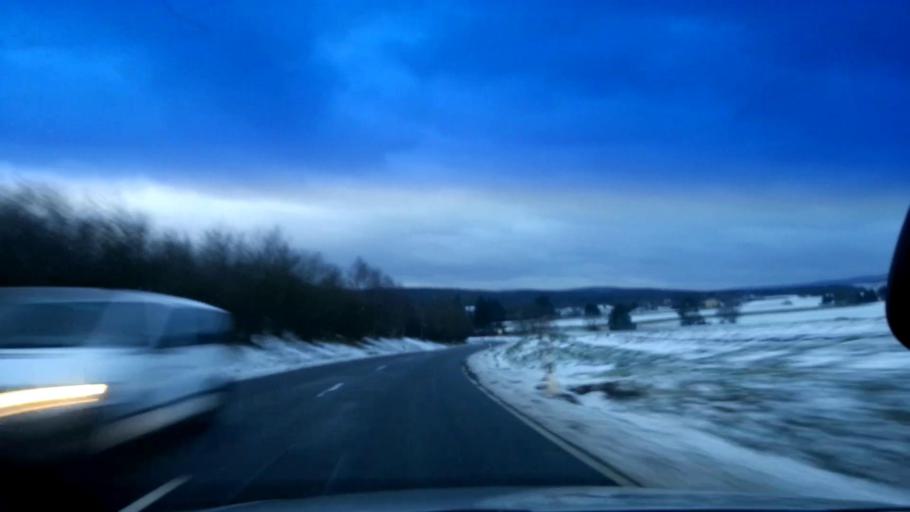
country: DE
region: Bavaria
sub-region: Upper Franconia
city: Marktleuthen
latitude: 50.1338
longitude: 12.0057
